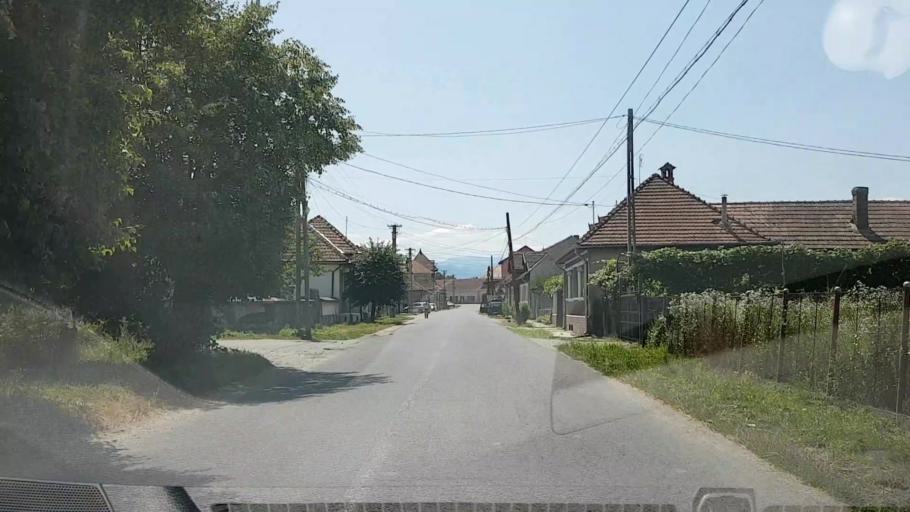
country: RO
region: Brasov
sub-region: Comuna Voila
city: Voila
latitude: 45.8198
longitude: 24.8395
